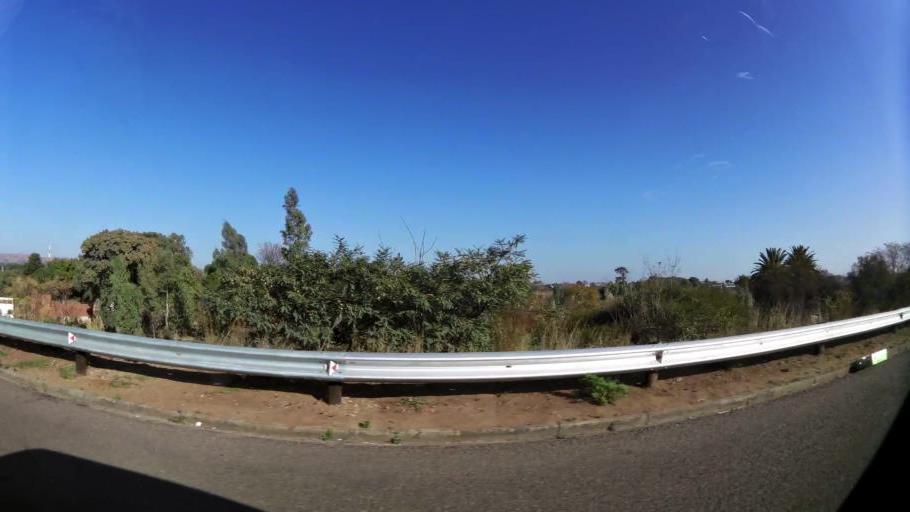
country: ZA
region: North-West
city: Ga-Rankuwa
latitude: -25.6389
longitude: 28.1113
